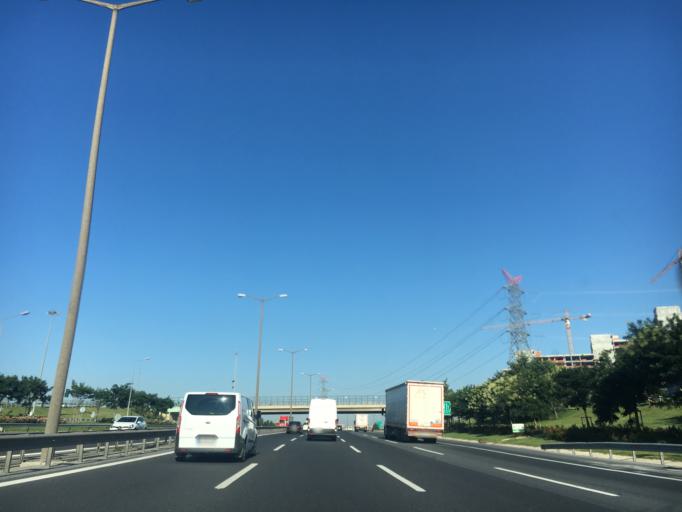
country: TR
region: Istanbul
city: Esenyurt
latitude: 41.0539
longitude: 28.6732
